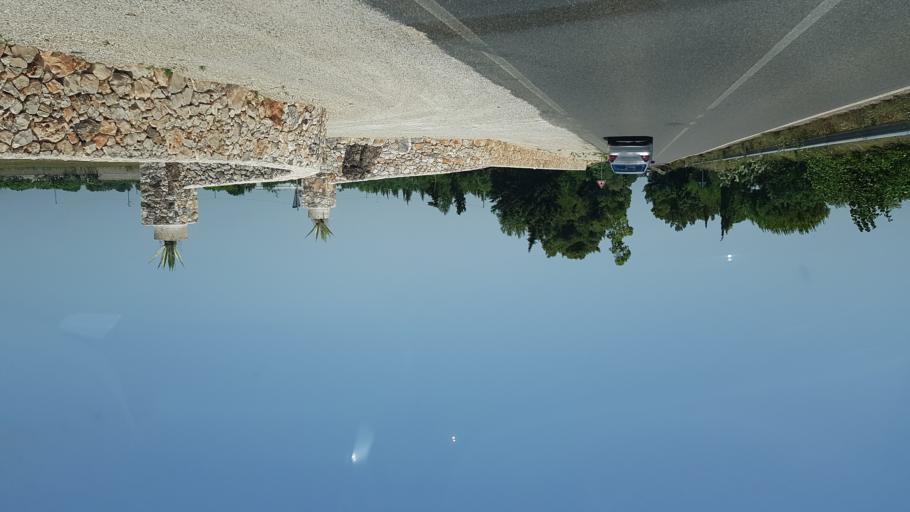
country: IT
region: Apulia
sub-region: Provincia di Lecce
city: Porto Cesareo
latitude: 40.2698
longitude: 17.9073
